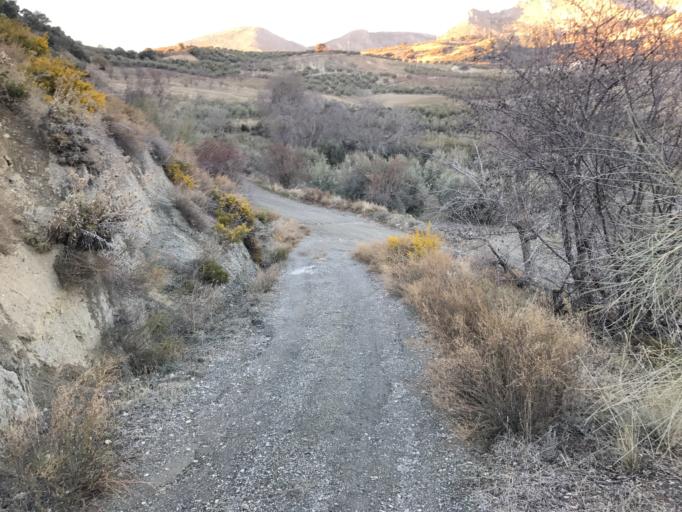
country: ES
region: Andalusia
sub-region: Provincia de Granada
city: Beas de Granada
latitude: 37.2177
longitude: -3.4871
